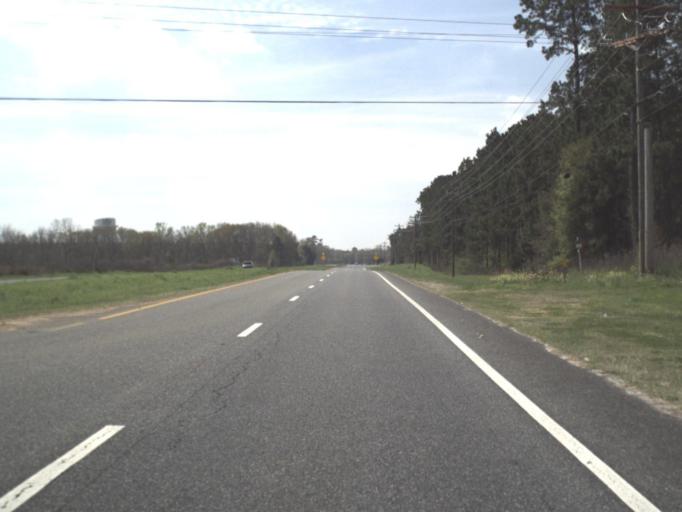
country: US
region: Florida
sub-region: Gadsden County
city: Havana
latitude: 30.6605
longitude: -84.4120
